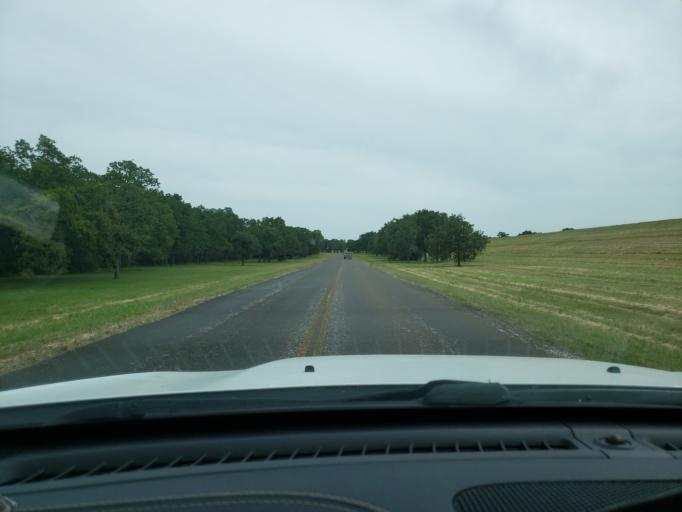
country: US
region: Texas
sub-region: Burleson County
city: Somerville
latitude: 30.3427
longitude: -96.5444
